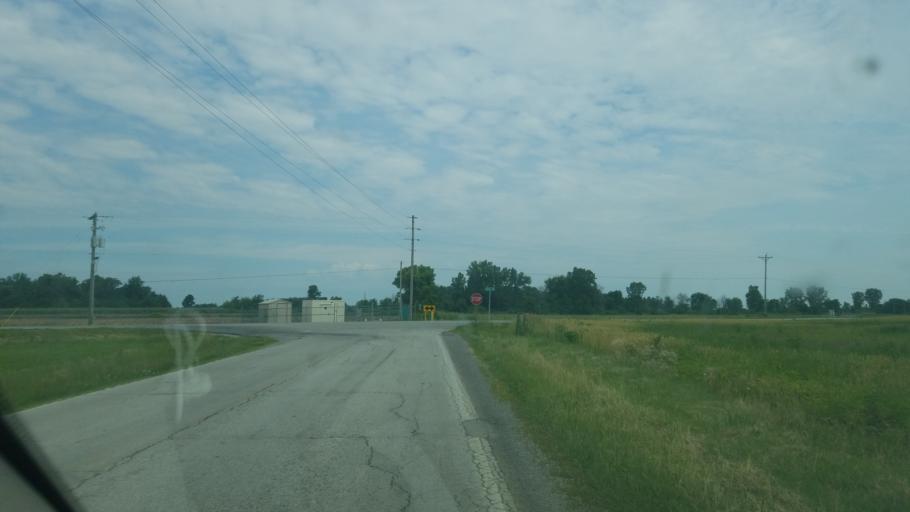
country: US
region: Ohio
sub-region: Seneca County
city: Fostoria
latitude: 41.1256
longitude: -83.4787
